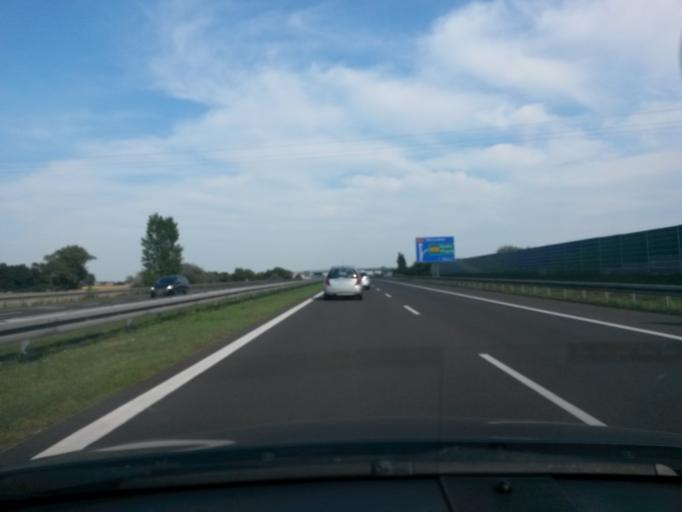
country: PL
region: Greater Poland Voivodeship
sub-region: Powiat slupecki
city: Strzalkowo
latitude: 52.2598
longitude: 17.7886
